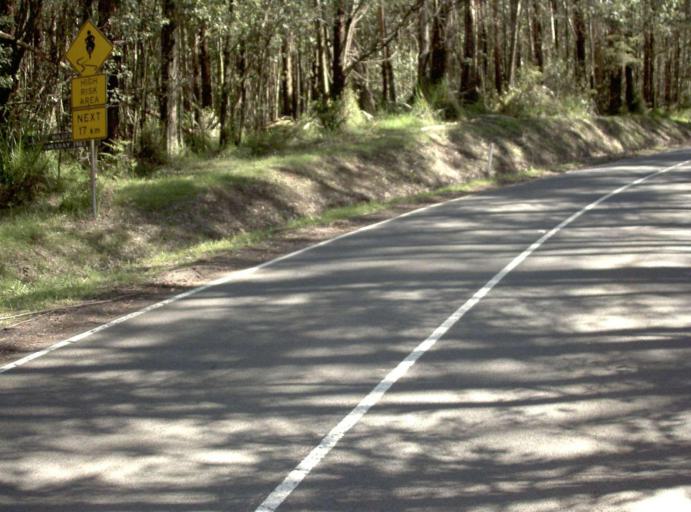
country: AU
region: Victoria
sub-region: Yarra Ranges
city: Millgrove
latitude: -37.8714
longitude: 145.8046
